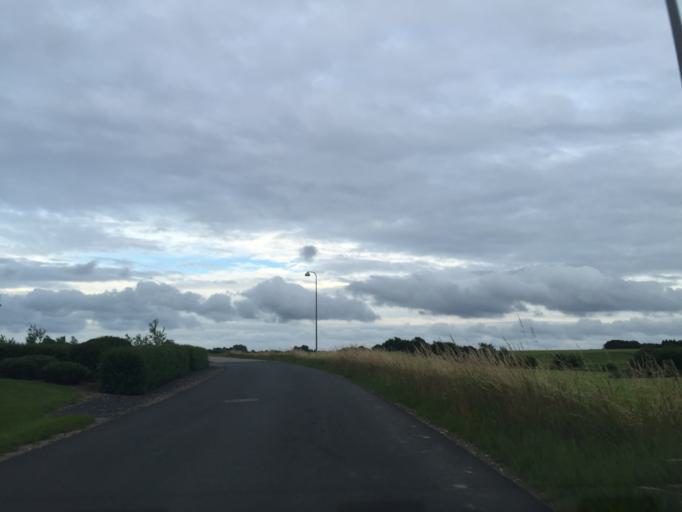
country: DK
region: Central Jutland
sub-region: Silkeborg Kommune
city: Kjellerup
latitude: 56.2442
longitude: 9.4940
